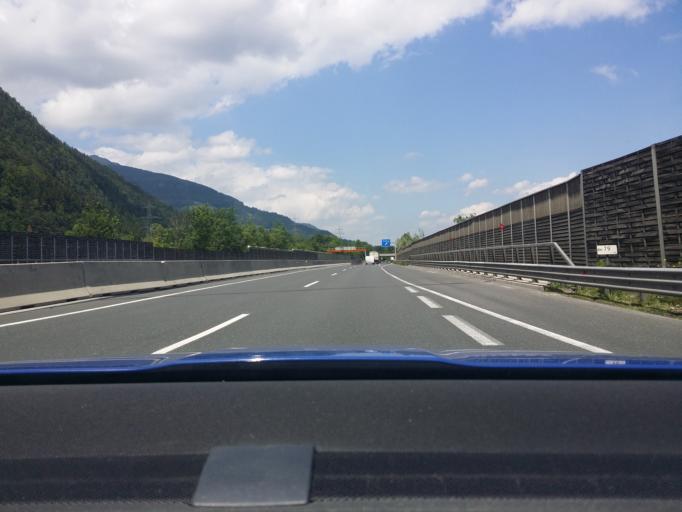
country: AT
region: Salzburg
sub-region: Politischer Bezirk Hallein
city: Golling an der Salzach
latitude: 47.5869
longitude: 13.1553
